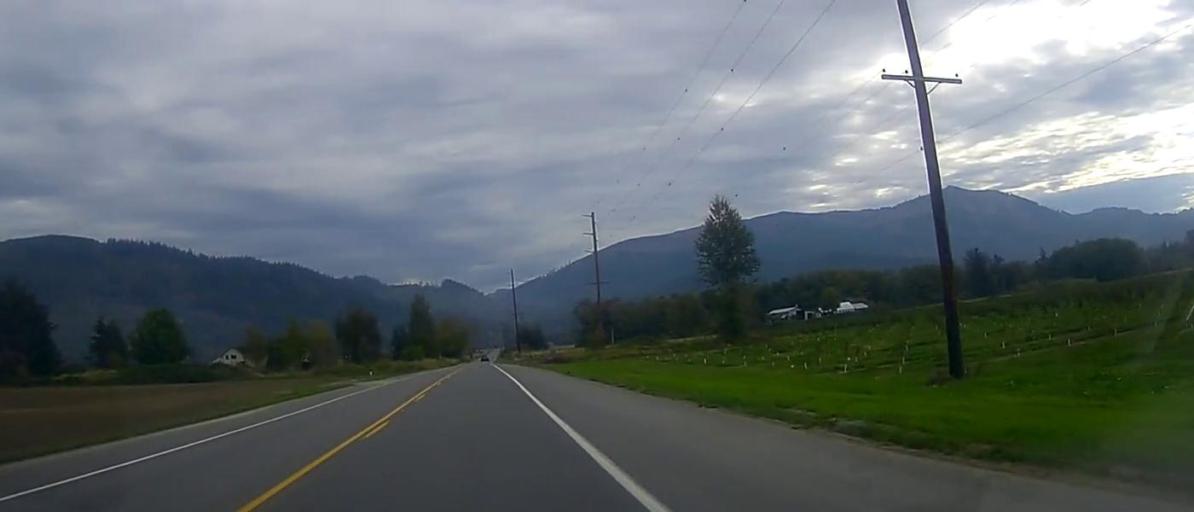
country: US
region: Washington
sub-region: Skagit County
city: Clear Lake
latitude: 48.4680
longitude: -122.2476
